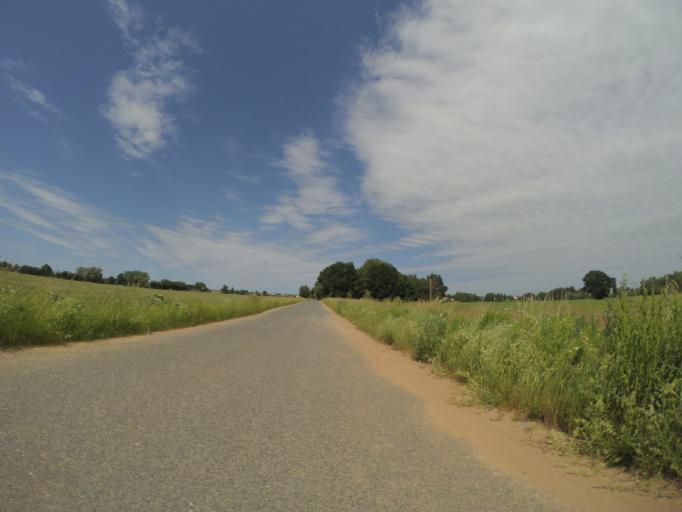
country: CZ
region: Central Bohemia
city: Milovice
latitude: 50.1749
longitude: 14.8863
